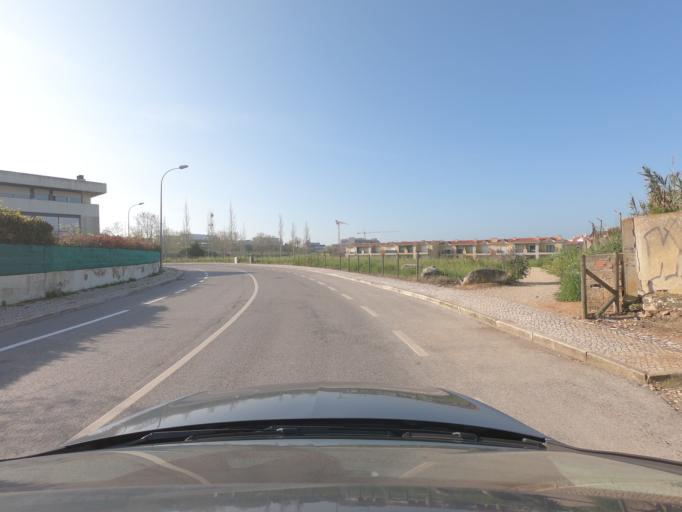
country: PT
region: Lisbon
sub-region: Oeiras
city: Carcavelos
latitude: 38.6824
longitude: -9.3245
